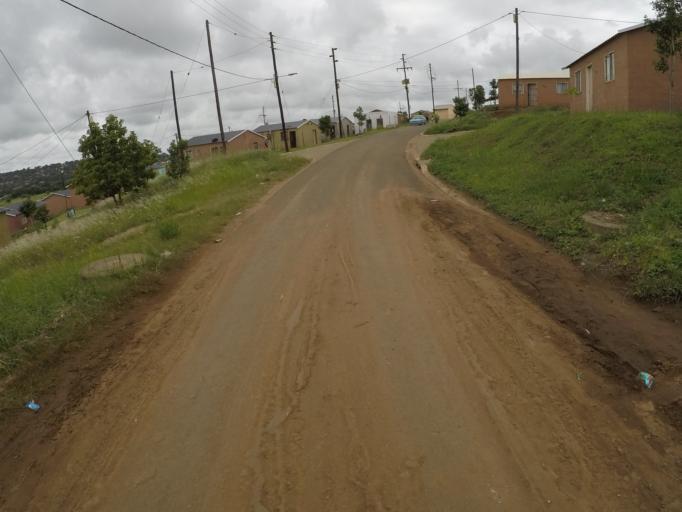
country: ZA
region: KwaZulu-Natal
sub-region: uThungulu District Municipality
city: Empangeni
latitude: -28.7618
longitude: 31.8762
